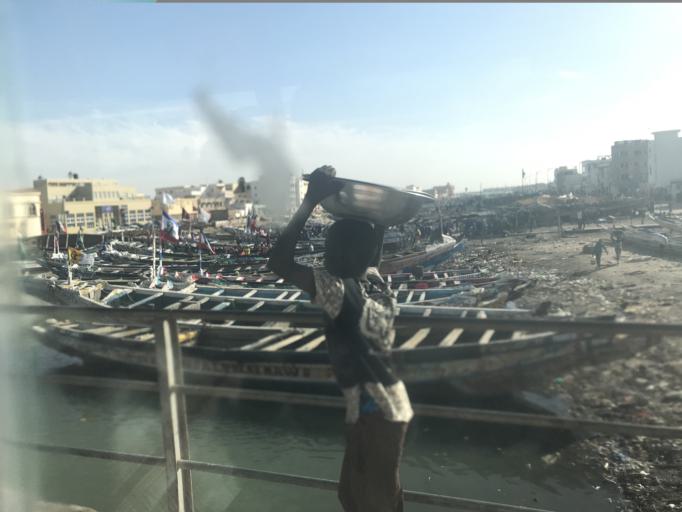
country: SN
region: Saint-Louis
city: Saint-Louis
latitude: 16.0260
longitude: -16.5070
